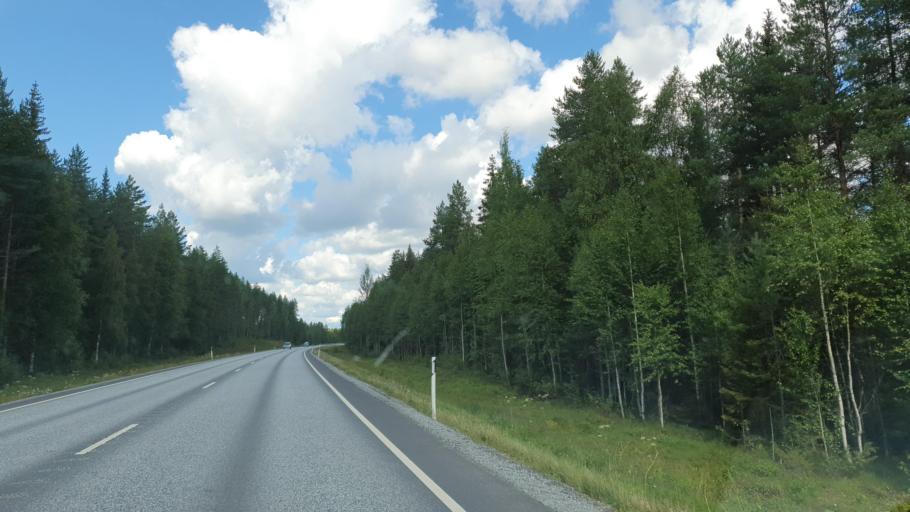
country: FI
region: Northern Savo
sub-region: Ylae-Savo
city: Sonkajaervi
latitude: 63.9067
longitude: 27.3888
